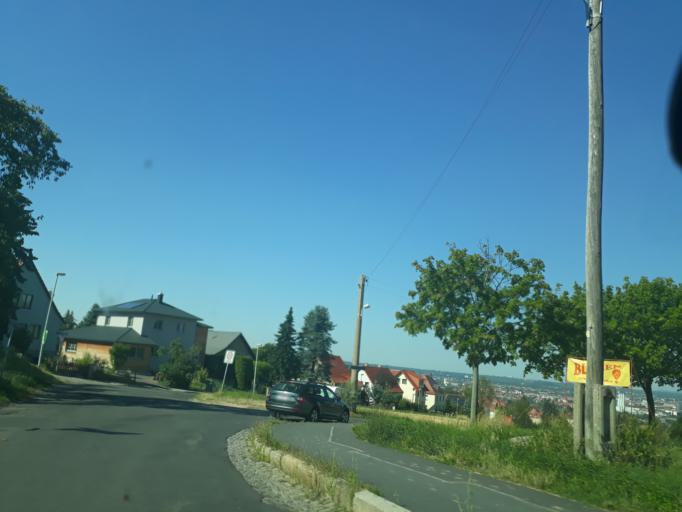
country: DE
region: Saxony
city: Bannewitz
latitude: 51.0253
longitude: 13.6889
